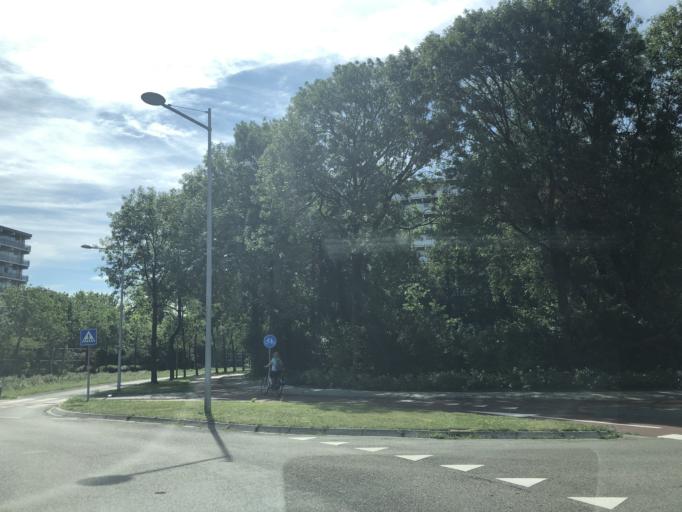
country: NL
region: Gelderland
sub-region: Gemeente Wageningen
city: Wageningen
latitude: 51.9766
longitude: 5.6613
